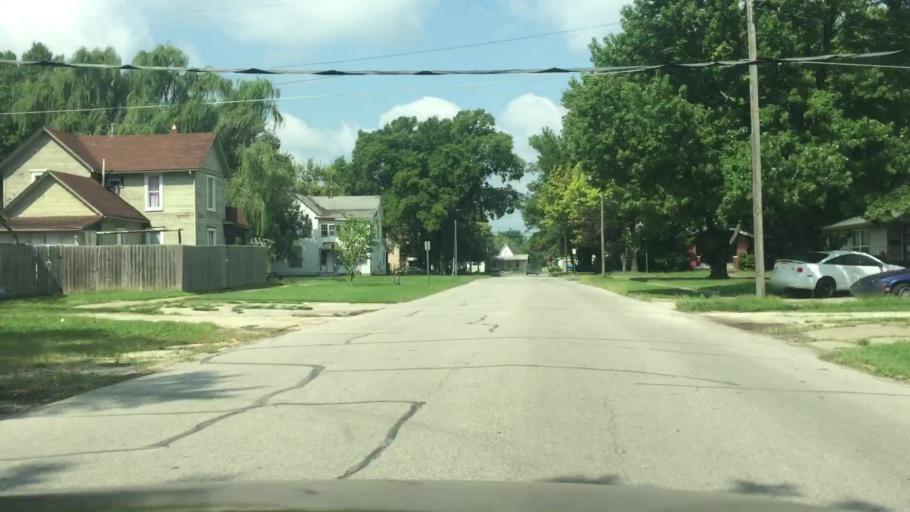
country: US
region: Kansas
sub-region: Allen County
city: Iola
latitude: 37.9200
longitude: -95.4071
